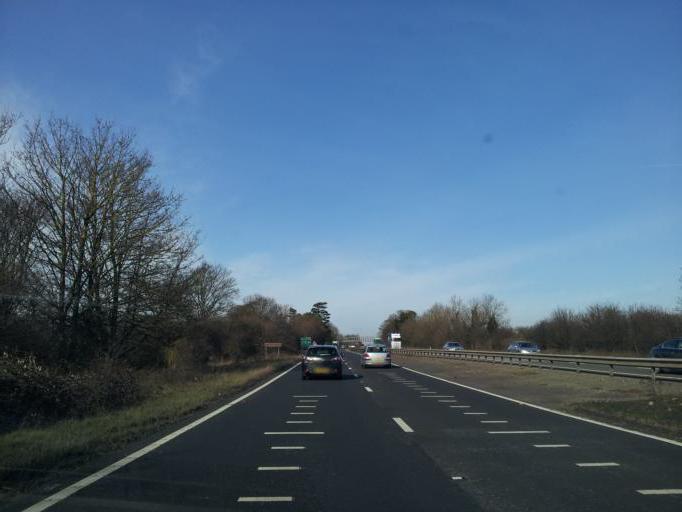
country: GB
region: England
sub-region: Lincolnshire
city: Grantham
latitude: 52.8580
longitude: -0.6290
